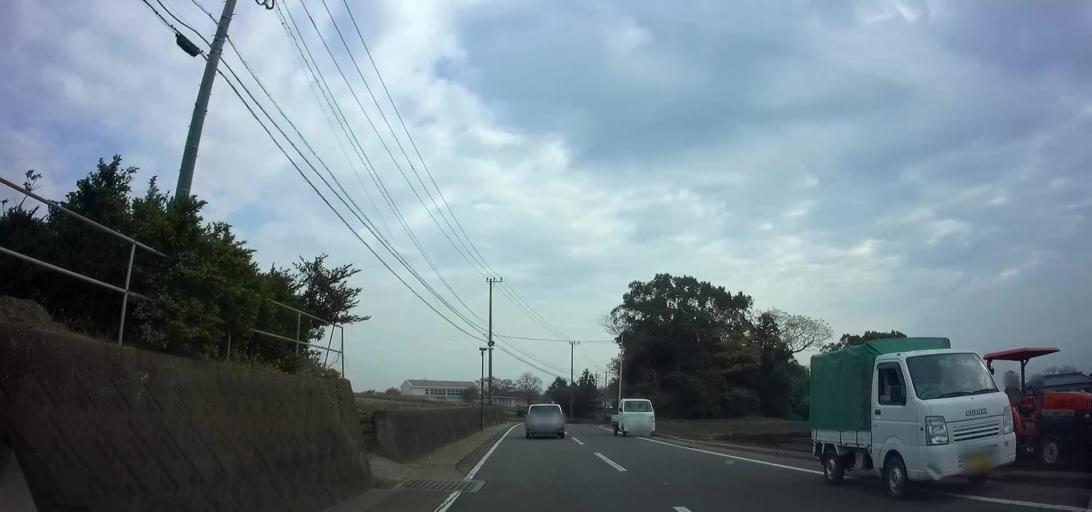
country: JP
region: Nagasaki
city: Shimabara
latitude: 32.6980
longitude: 130.3314
